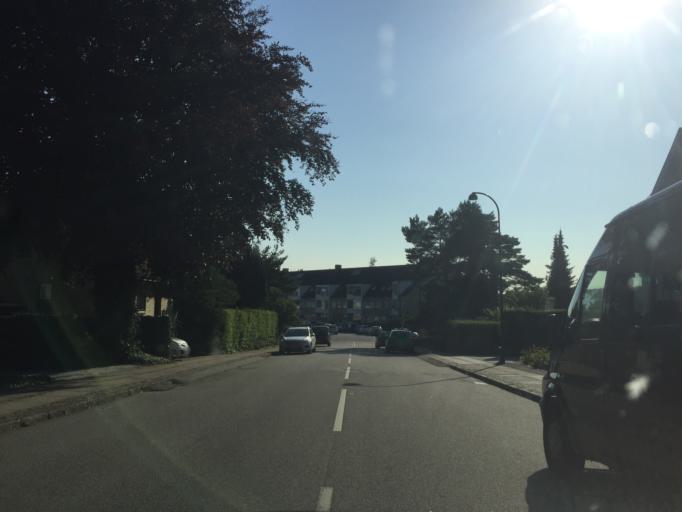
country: DK
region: Capital Region
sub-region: Lyngby-Tarbaek Kommune
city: Kongens Lyngby
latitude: 55.7641
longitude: 12.5247
